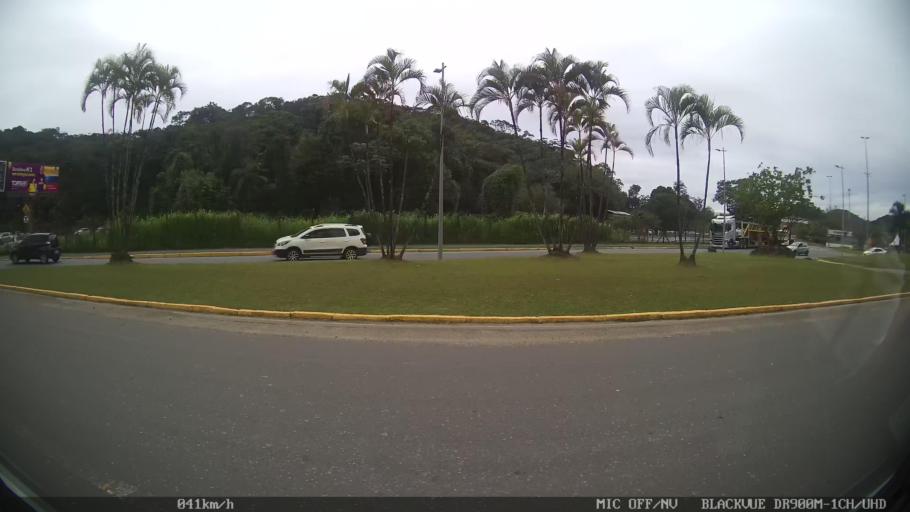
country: BR
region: Santa Catarina
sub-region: Joinville
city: Joinville
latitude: -26.2962
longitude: -48.8816
